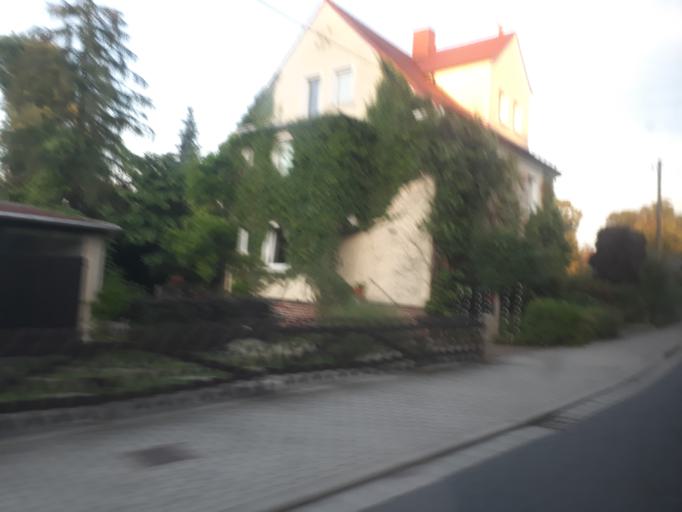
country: DE
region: Saxony
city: Radeberg
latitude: 51.0576
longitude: 13.8865
